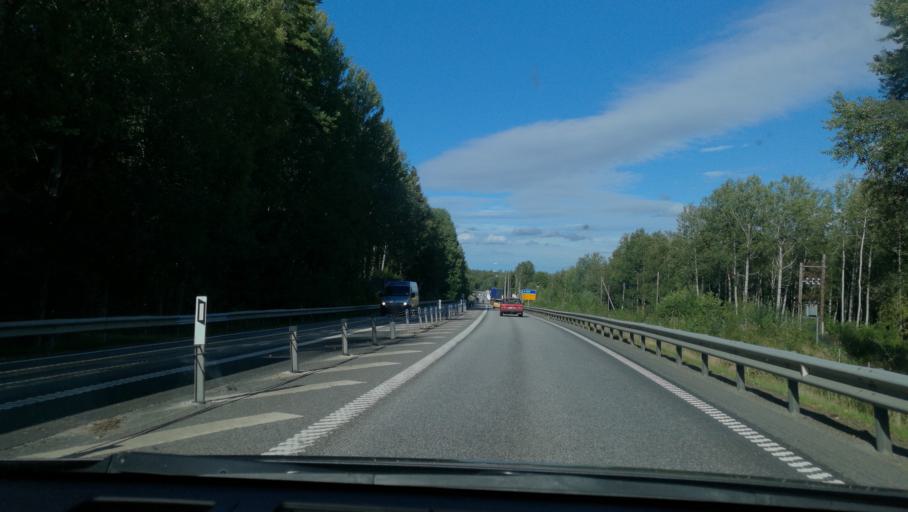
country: SE
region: OErebro
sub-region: Laxa Kommun
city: Laxa
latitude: 58.9635
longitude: 14.5344
